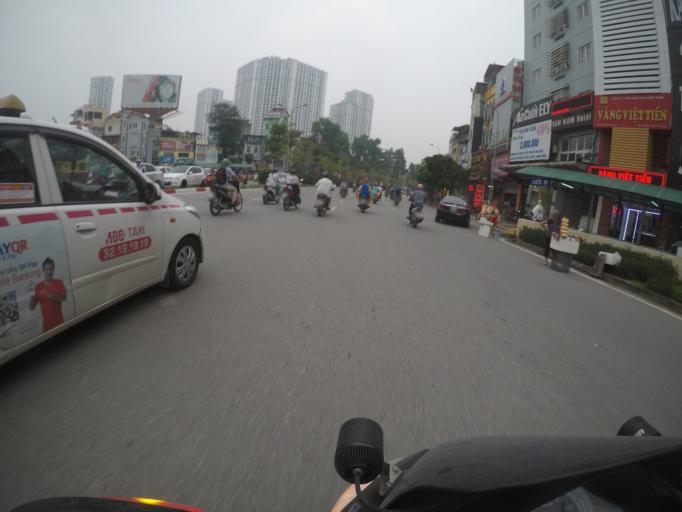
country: VN
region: Ha Noi
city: Dong Da
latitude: 21.0033
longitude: 105.8198
